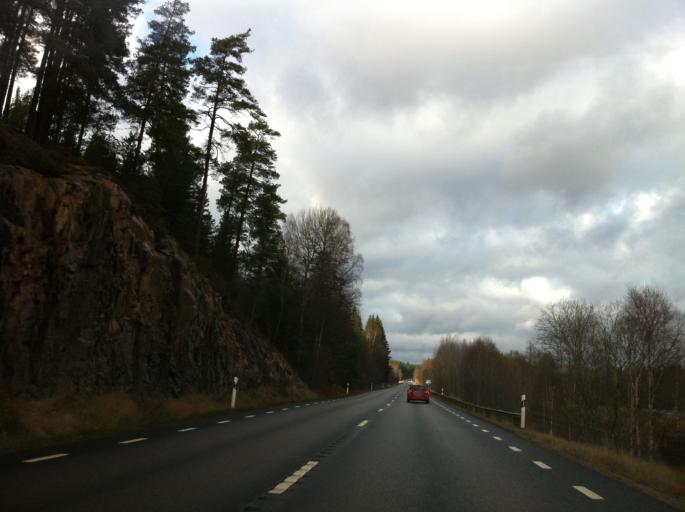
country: SE
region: Kalmar
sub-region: Hultsfreds Kommun
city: Hultsfred
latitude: 57.5342
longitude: 15.8169
